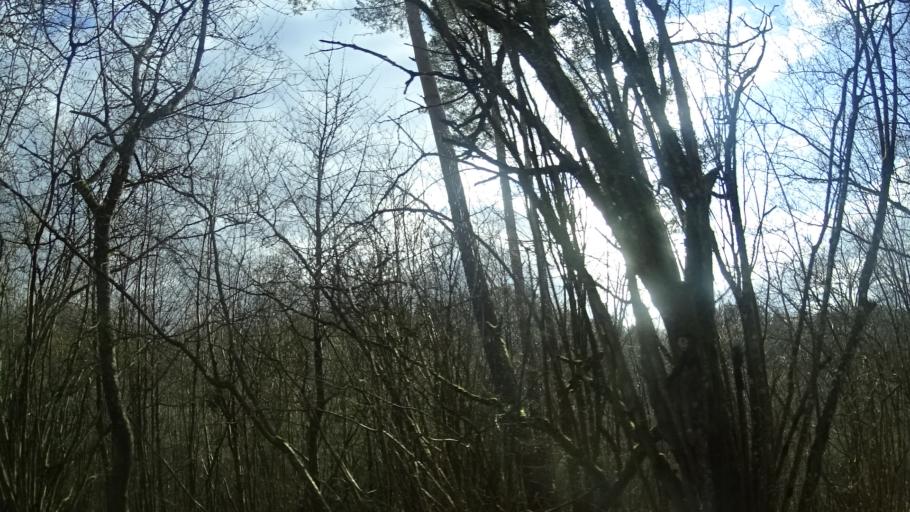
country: DE
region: Rheinland-Pfalz
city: Kronweiler
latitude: 49.6534
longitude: 7.2698
